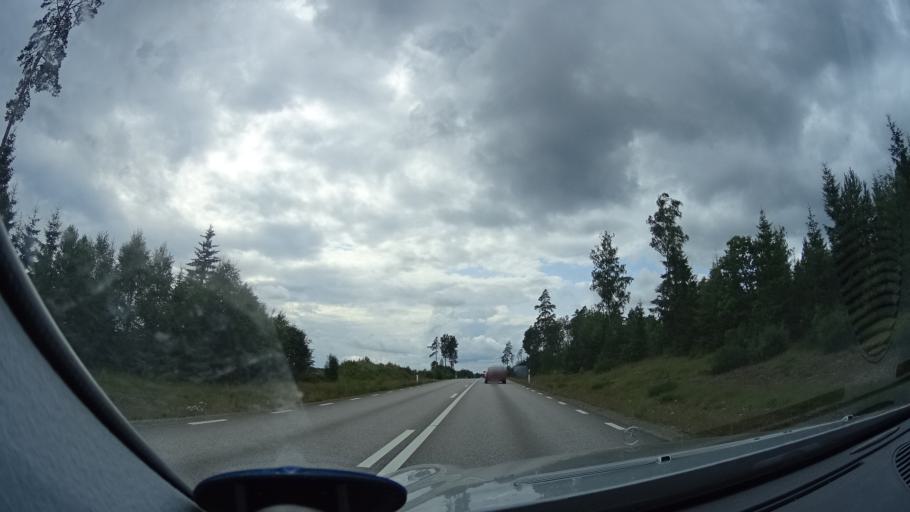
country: SE
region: Kronoberg
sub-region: Tingsryds Kommun
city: Tingsryd
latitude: 56.5115
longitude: 15.0095
